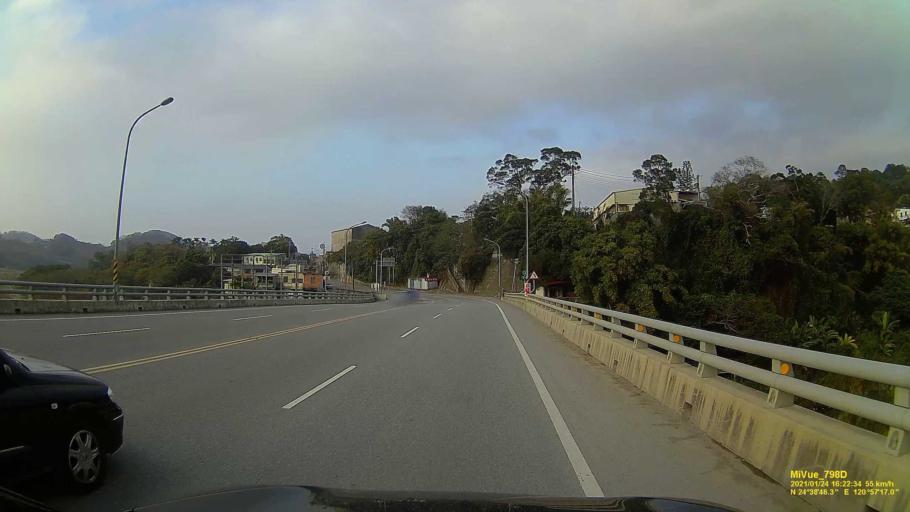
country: TW
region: Taiwan
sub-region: Miaoli
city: Miaoli
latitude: 24.6465
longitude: 120.9548
